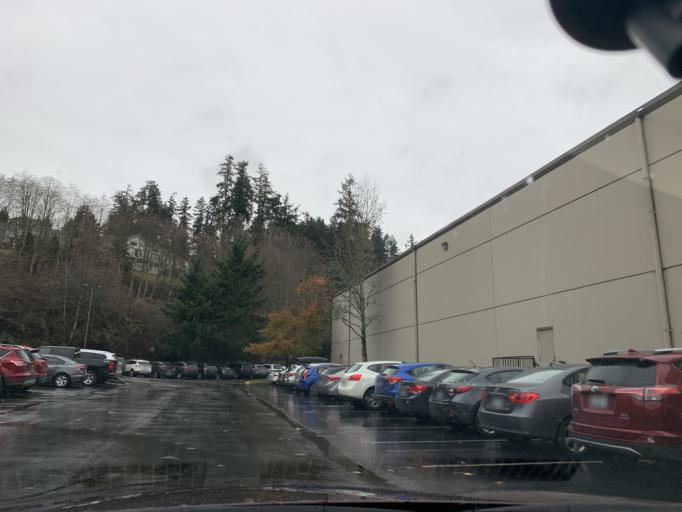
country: US
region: Washington
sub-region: King County
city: Woodinville
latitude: 47.7407
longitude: -122.1594
